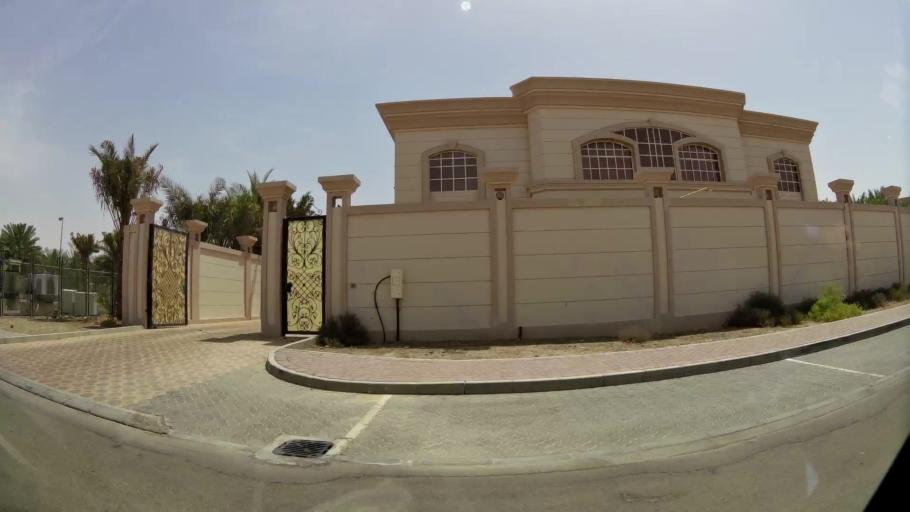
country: AE
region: Abu Dhabi
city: Al Ain
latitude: 24.1784
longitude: 55.7134
